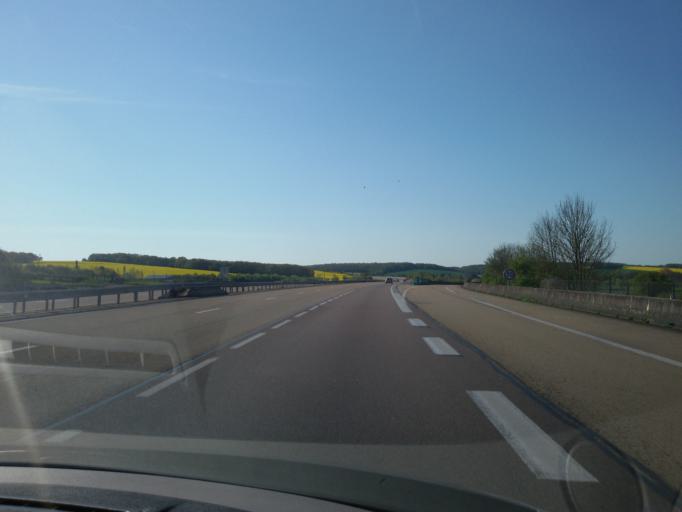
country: FR
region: Bourgogne
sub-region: Departement de l'Yonne
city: Saint-Julien-du-Sault
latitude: 47.9436
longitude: 3.2405
